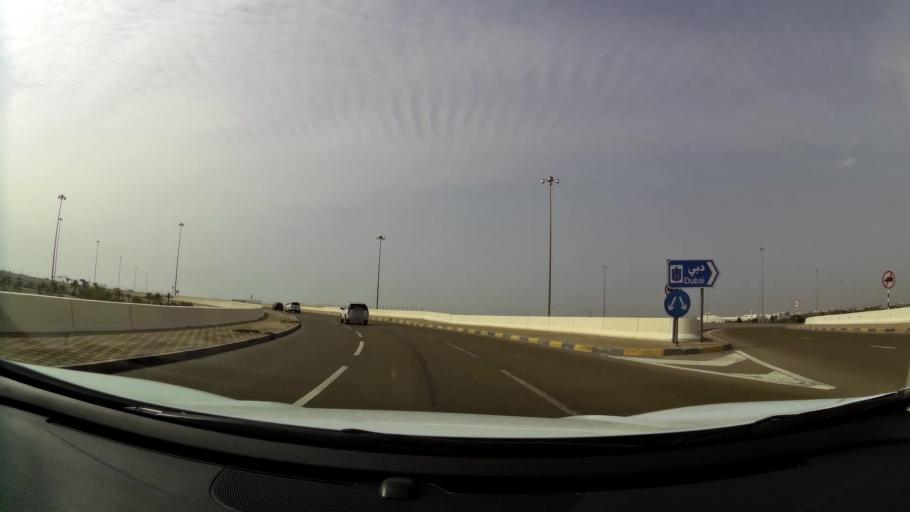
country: AE
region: Abu Dhabi
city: Abu Dhabi
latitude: 24.5647
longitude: 54.6968
